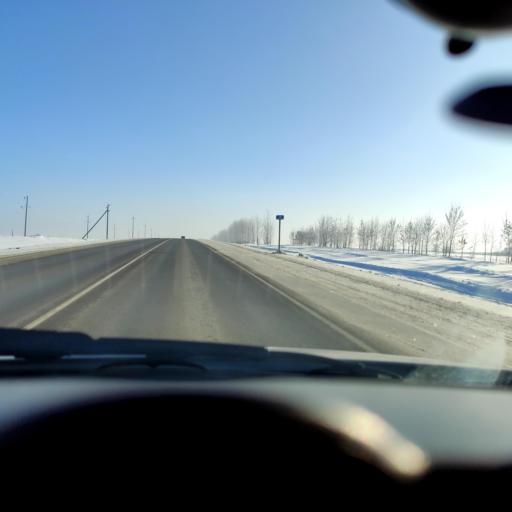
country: RU
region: Kursk
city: Tim
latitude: 51.6544
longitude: 36.9273
